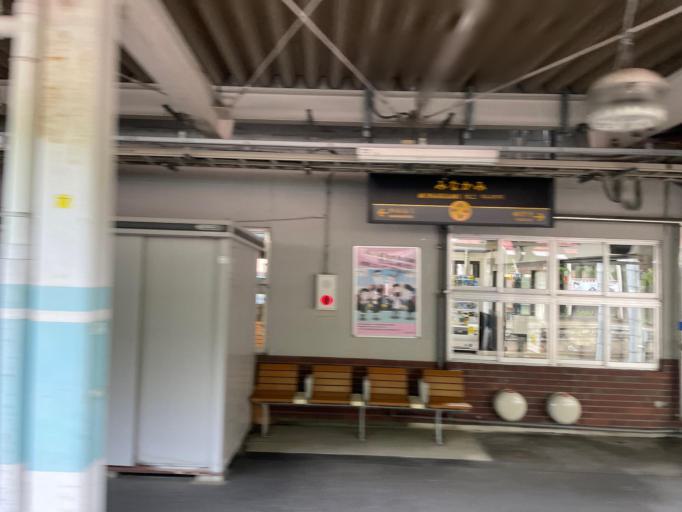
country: JP
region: Gunma
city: Numata
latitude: 36.7785
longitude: 138.9690
